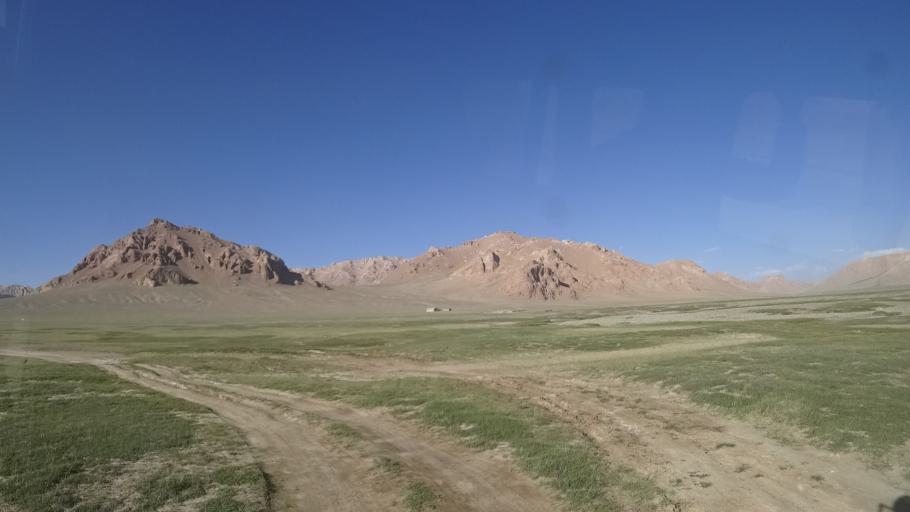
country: TJ
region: Gorno-Badakhshan
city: Murghob
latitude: 37.6619
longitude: 74.1707
